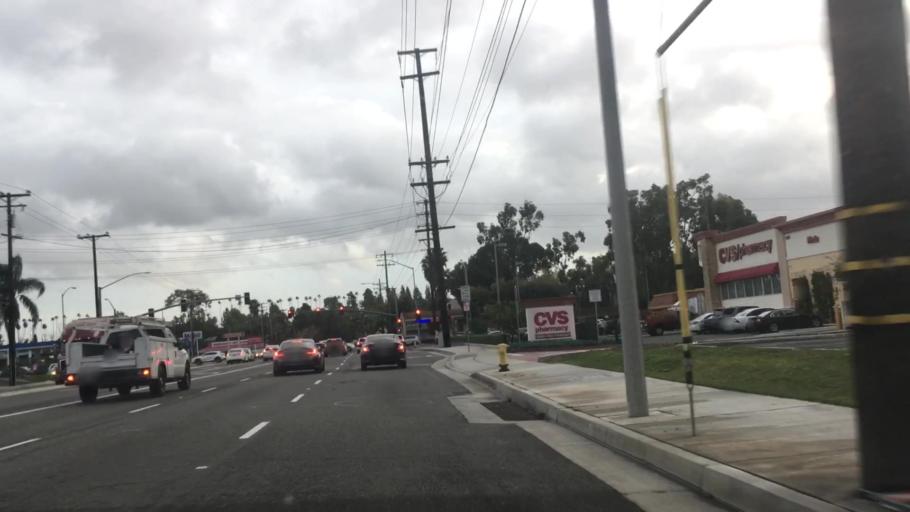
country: US
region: California
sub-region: Orange County
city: La Habra
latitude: 33.9183
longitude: -117.9332
